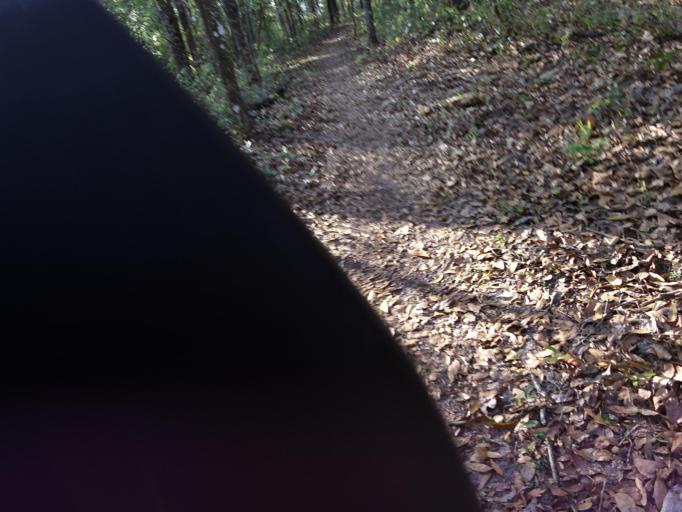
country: US
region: Florida
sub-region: Clay County
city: Middleburg
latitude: 30.1481
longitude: -81.9552
